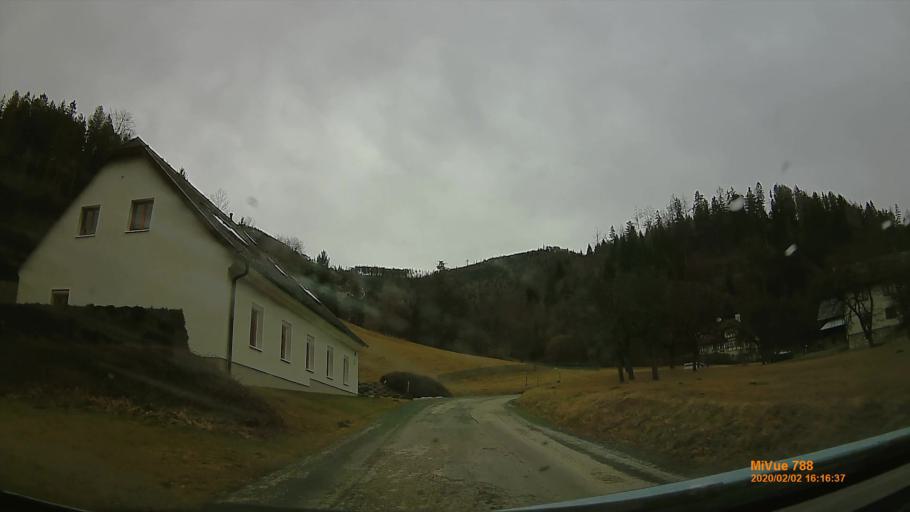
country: AT
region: Lower Austria
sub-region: Politischer Bezirk Neunkirchen
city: Semmering
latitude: 47.6507
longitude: 15.8152
